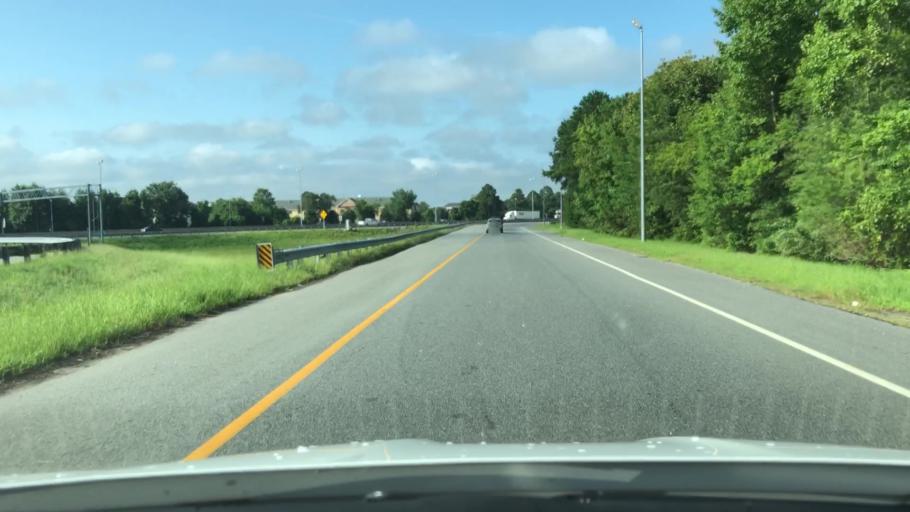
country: US
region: Virginia
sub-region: City of Chesapeake
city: Chesapeake
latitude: 36.7848
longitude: -76.2367
